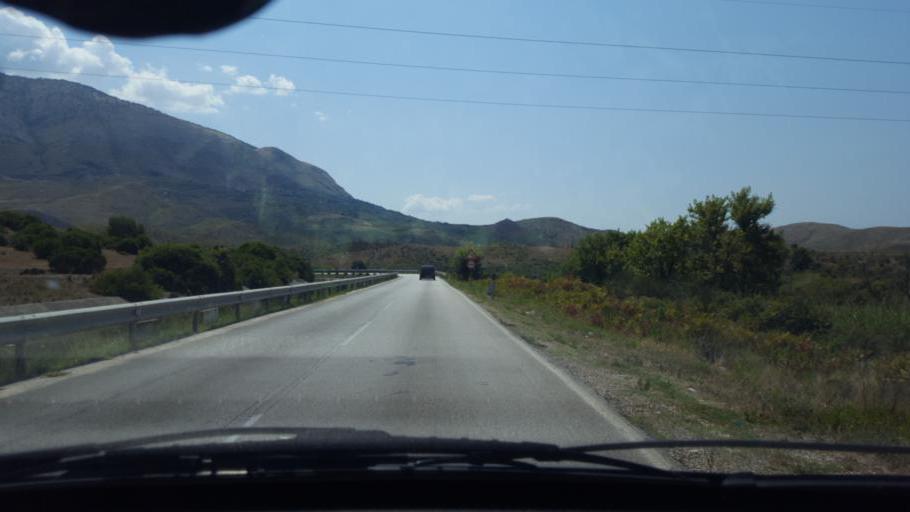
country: AL
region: Vlore
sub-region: Rrethi i Delvines
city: Mesopotam
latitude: 39.9100
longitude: 20.1229
